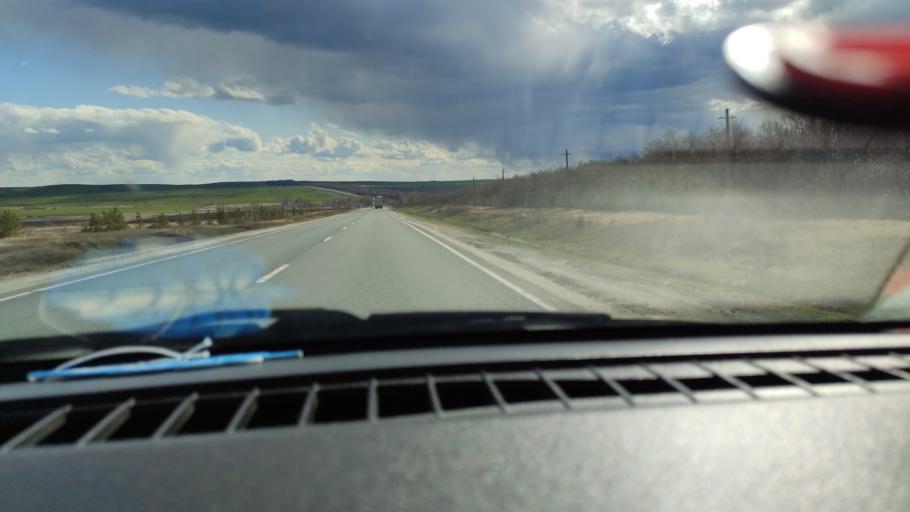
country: RU
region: Saratov
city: Alekseyevka
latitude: 52.2541
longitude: 47.9150
